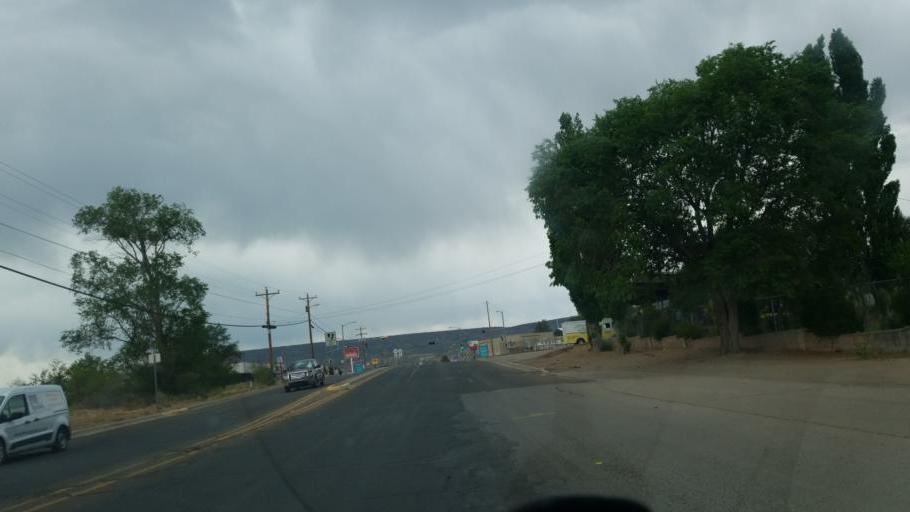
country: US
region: New Mexico
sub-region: Cibola County
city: Grants
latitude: 35.1611
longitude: -107.8357
